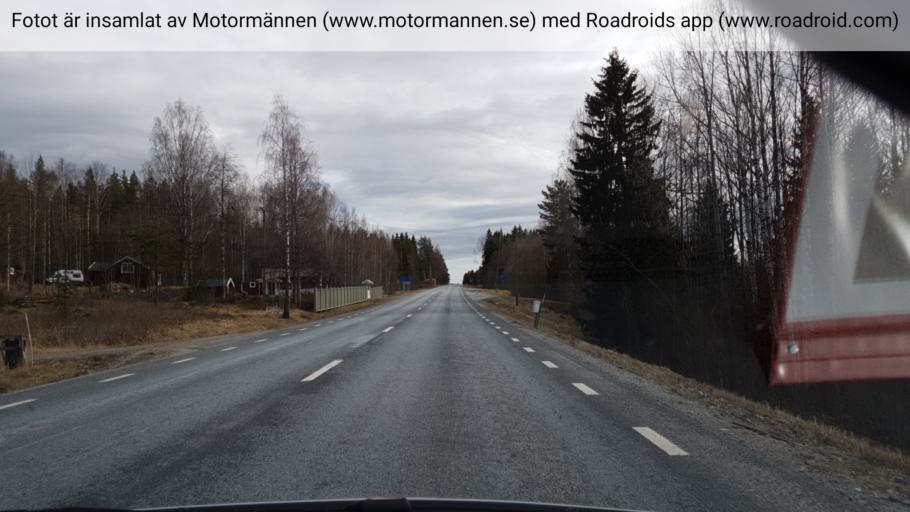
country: SE
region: Vaesternorrland
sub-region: Solleftea Kommun
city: Solleftea
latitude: 63.3927
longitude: 16.9786
